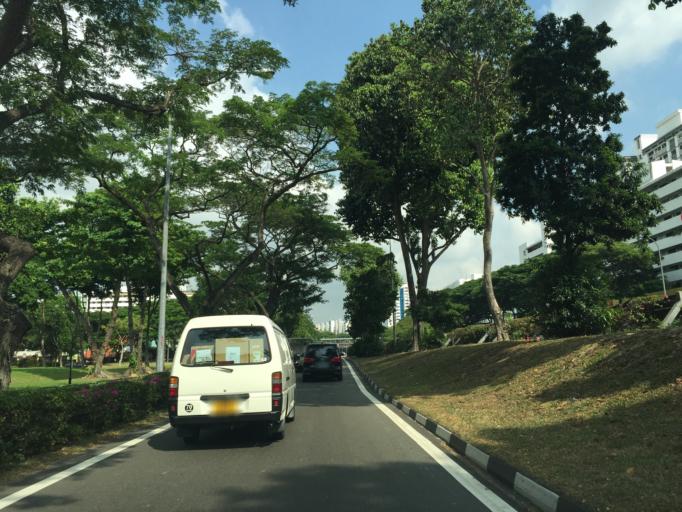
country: SG
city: Singapore
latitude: 1.3223
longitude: 103.8890
